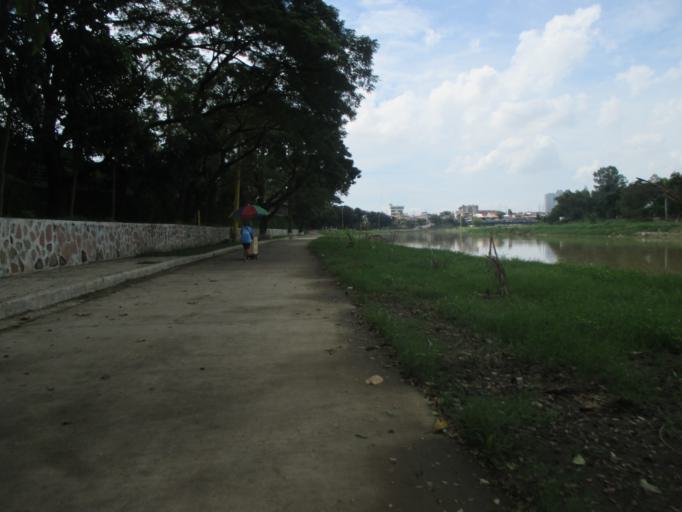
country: PH
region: Metro Manila
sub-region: Marikina
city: Calumpang
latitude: 14.6287
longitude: 121.0945
